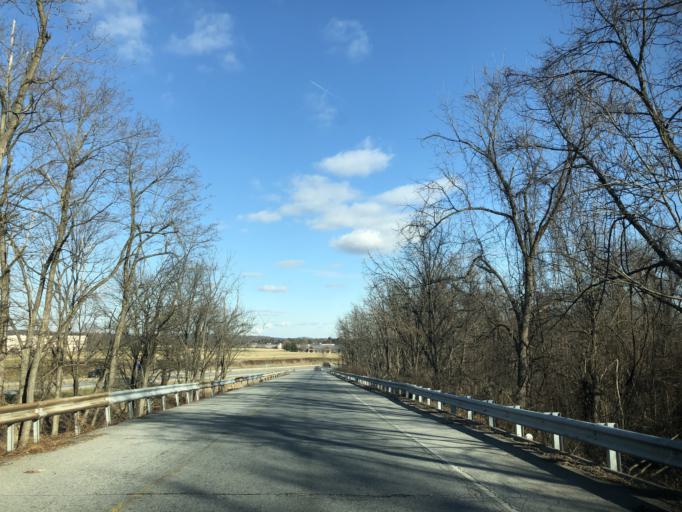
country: US
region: Pennsylvania
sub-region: Chester County
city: Coatesville
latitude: 39.9884
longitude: -75.8722
